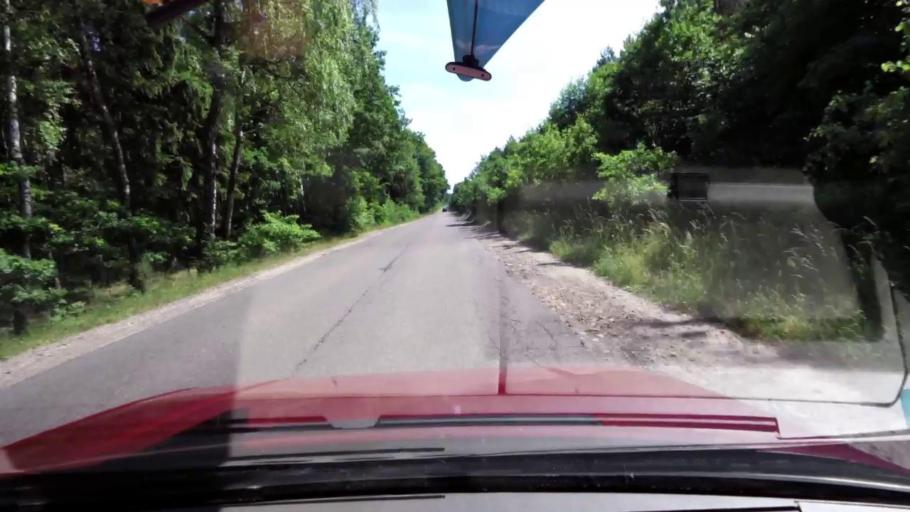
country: PL
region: Pomeranian Voivodeship
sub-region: Powiat slupski
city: Kepice
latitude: 54.3286
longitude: 16.9620
